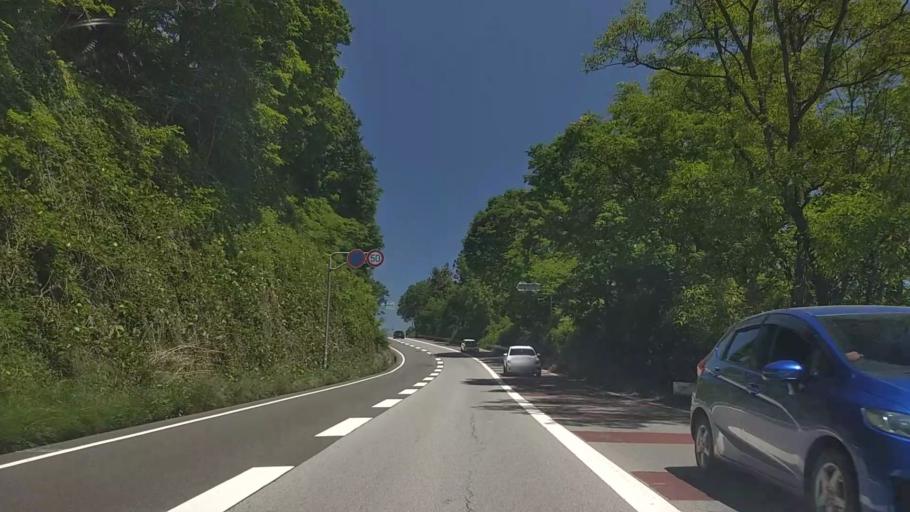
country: JP
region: Yamanashi
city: Nirasaki
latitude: 35.8054
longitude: 138.4276
